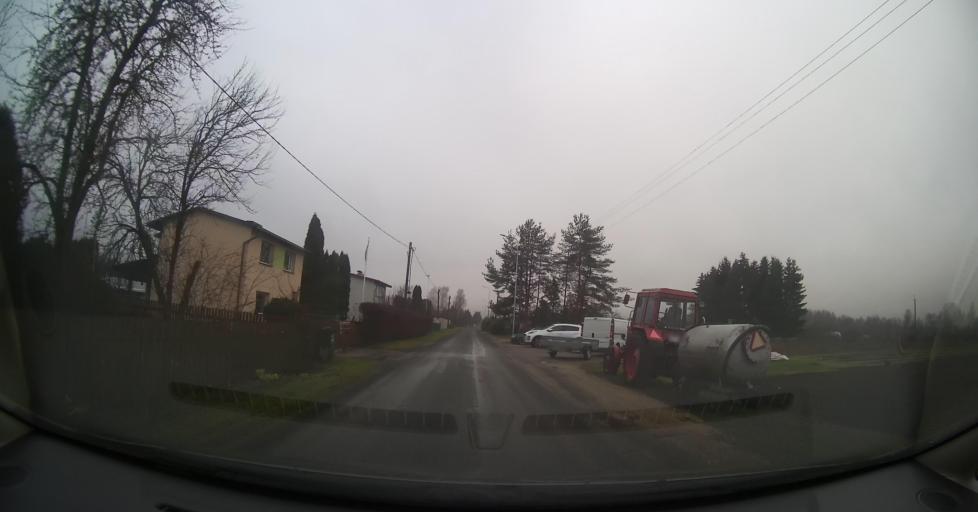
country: EE
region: Tartu
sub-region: Alatskivi vald
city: Kallaste
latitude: 58.3802
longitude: 27.0410
